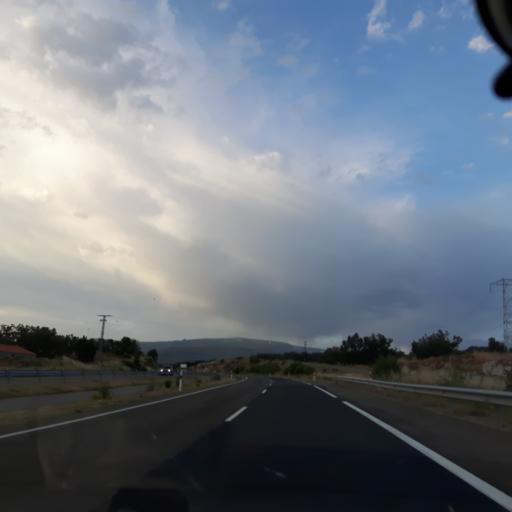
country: ES
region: Castille and Leon
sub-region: Provincia de Salamanca
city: Nava de Bejar
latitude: 40.4750
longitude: -5.6820
